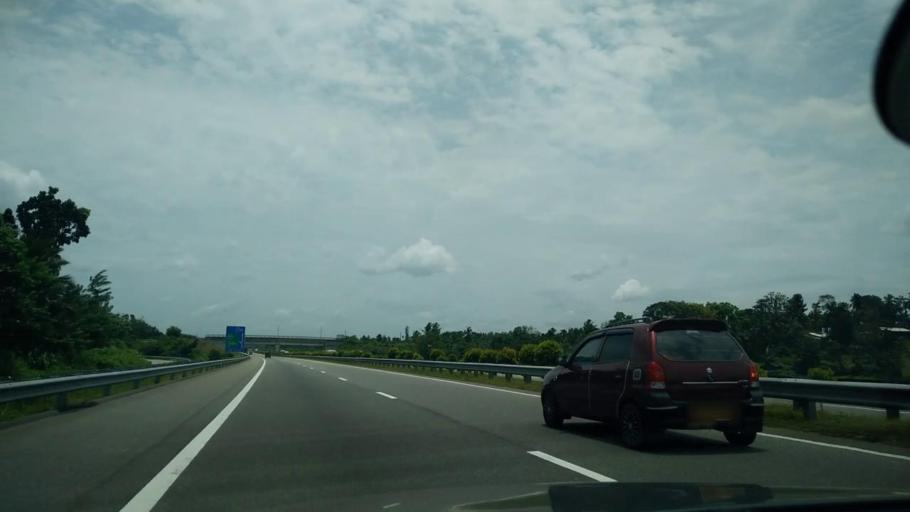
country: LK
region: Western
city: Homagama
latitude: 6.8711
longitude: 79.9782
